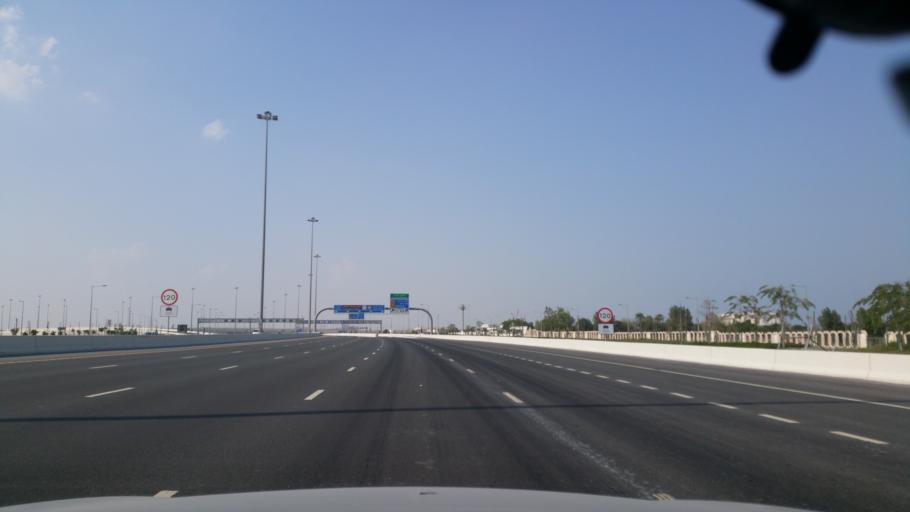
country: QA
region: Baladiyat Umm Salal
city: Umm Salal Muhammad
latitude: 25.3855
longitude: 51.5003
